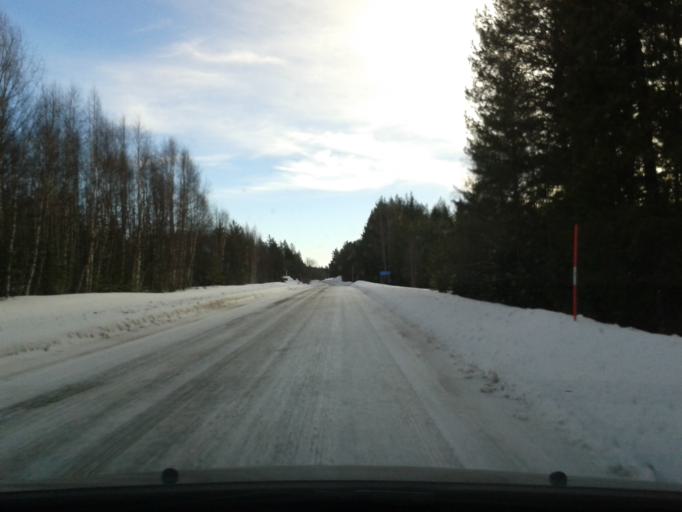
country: SE
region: Vaesterbotten
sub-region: Asele Kommun
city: Asele
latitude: 64.2274
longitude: 17.3021
